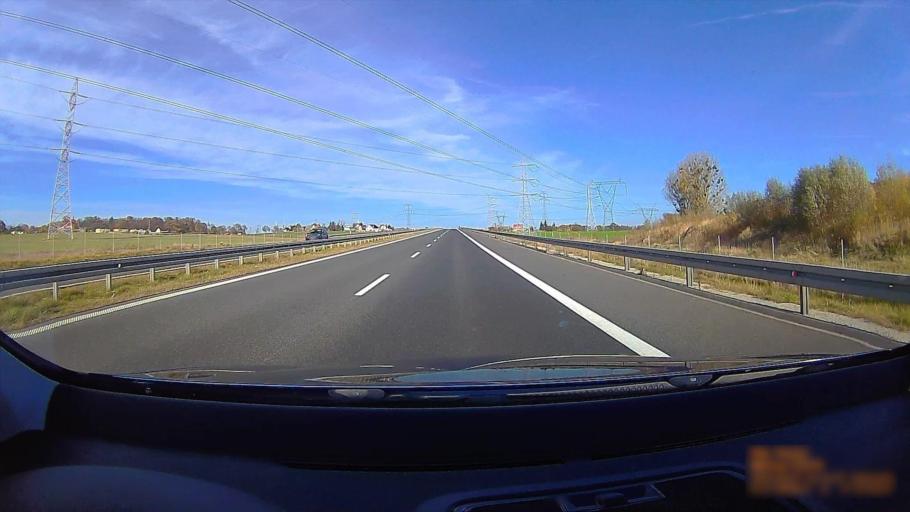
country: PL
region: Greater Poland Voivodeship
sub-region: Powiat ostrowski
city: Przygodzice
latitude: 51.6164
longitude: 17.8600
